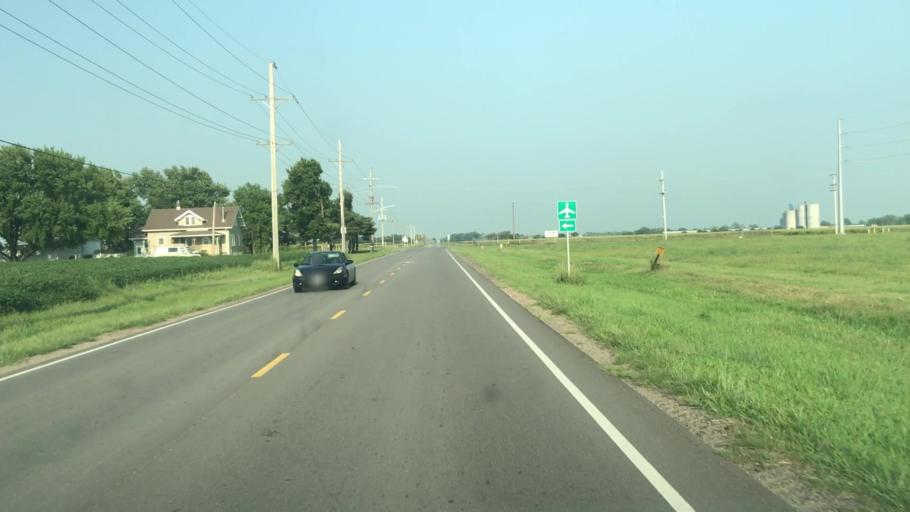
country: US
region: Nebraska
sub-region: Hall County
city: Grand Island
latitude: 40.9455
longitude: -98.3224
